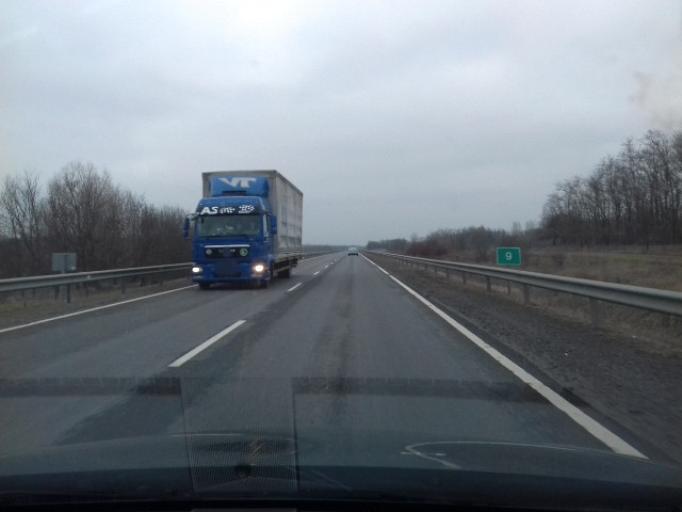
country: HU
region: Szabolcs-Szatmar-Bereg
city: Nyirpazony
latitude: 47.9727
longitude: 21.8175
